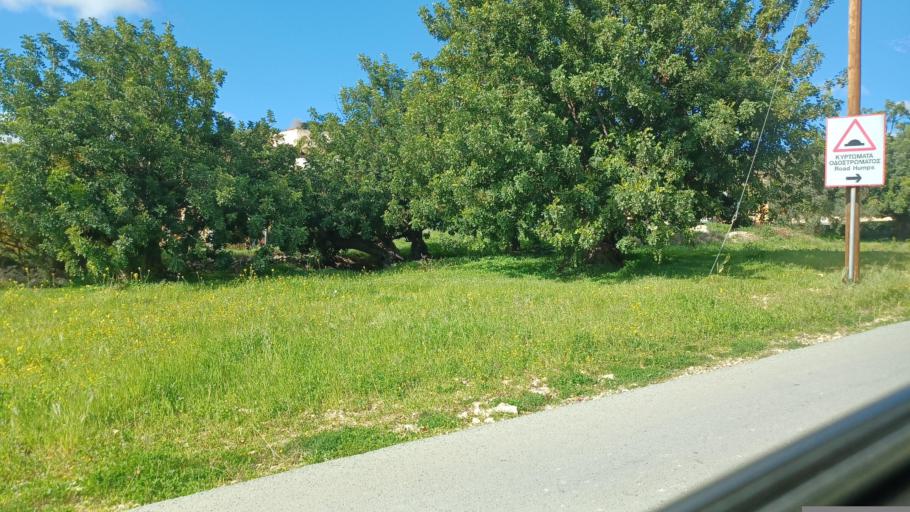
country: CY
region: Limassol
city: Pano Polemidia
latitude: 34.7890
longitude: 32.9766
